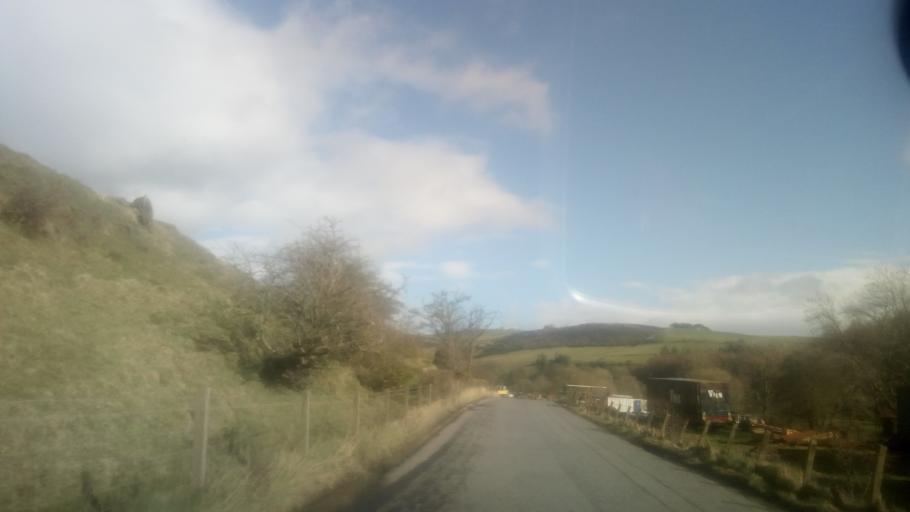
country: GB
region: Scotland
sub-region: The Scottish Borders
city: Hawick
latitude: 55.4109
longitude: -2.8358
